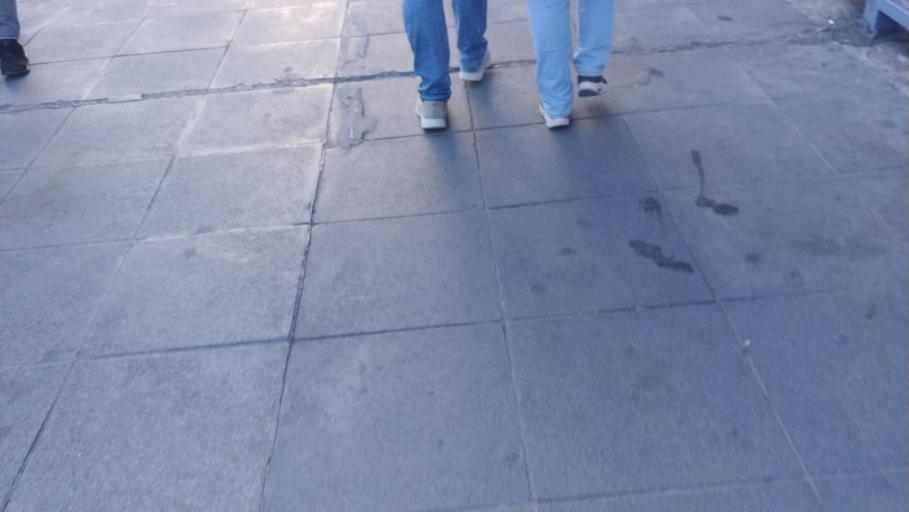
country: TR
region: Istanbul
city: Bahcelievler
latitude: 40.9925
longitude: 28.8387
